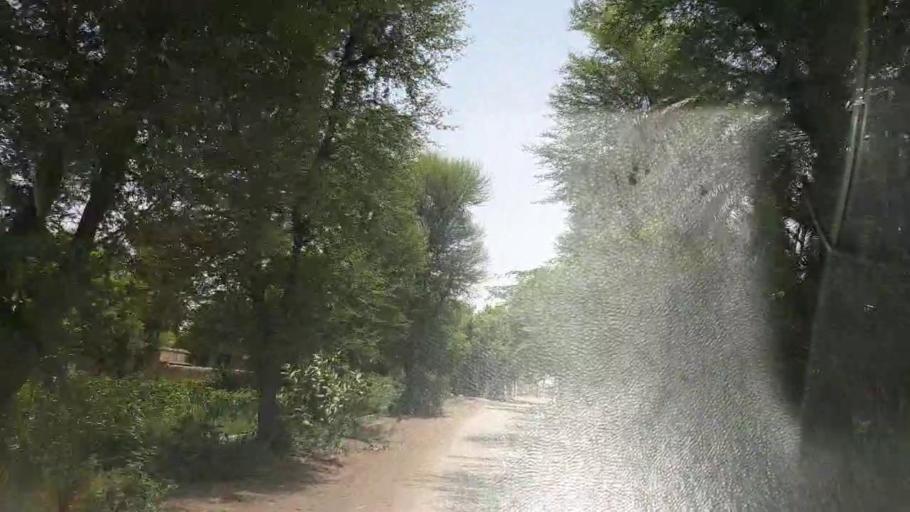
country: PK
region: Sindh
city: Bozdar
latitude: 27.2493
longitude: 68.6851
